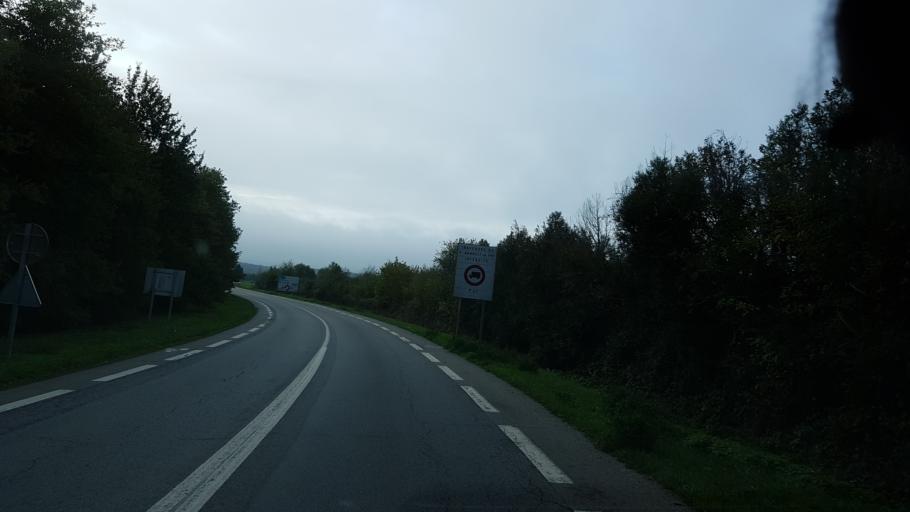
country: FR
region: Ile-de-France
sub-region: Departement des Yvelines
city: Bullion
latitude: 48.5848
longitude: 1.9807
